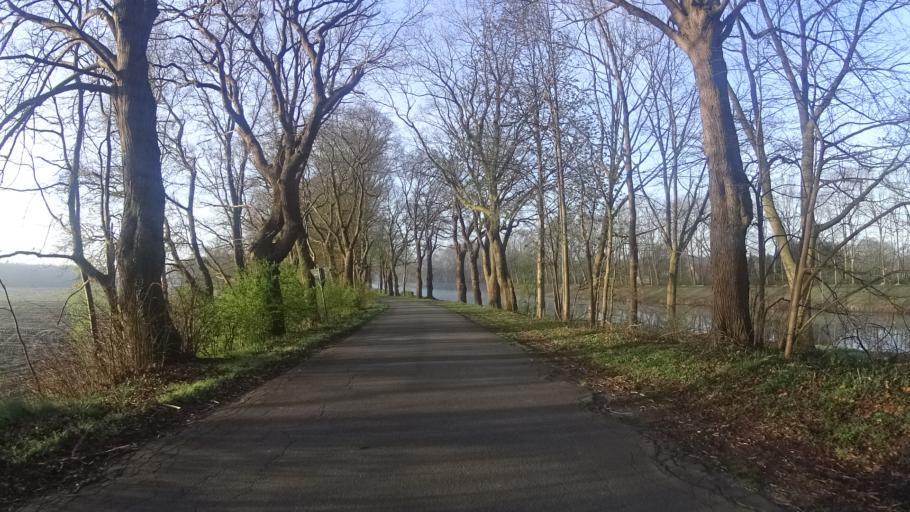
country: DE
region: Lower Saxony
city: Fresenburg
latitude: 52.8949
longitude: 7.3135
